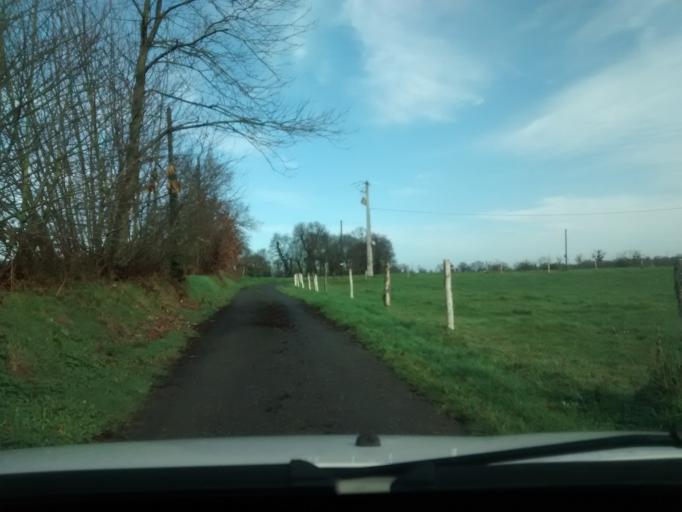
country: FR
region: Brittany
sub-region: Departement d'Ille-et-Vilaine
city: Vezin-le-Coquet
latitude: 48.1290
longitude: -1.7327
